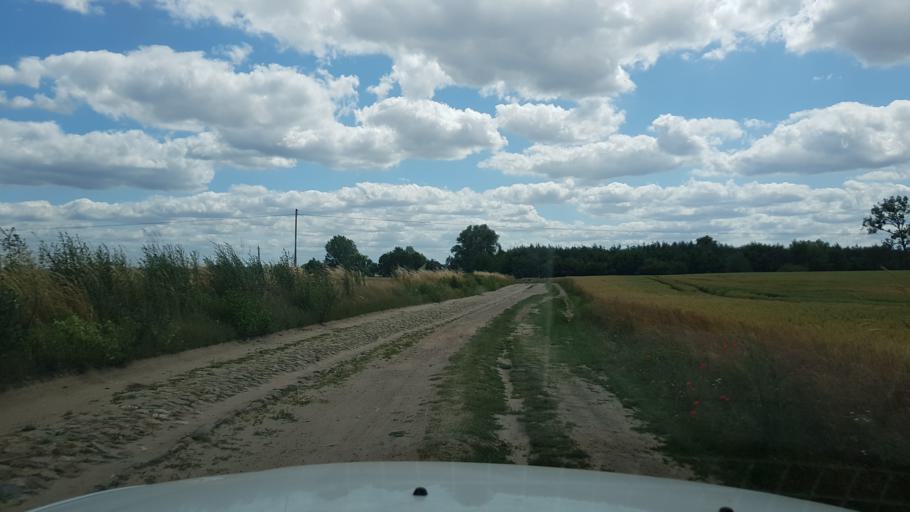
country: PL
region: West Pomeranian Voivodeship
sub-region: Powiat pyrzycki
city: Lipiany
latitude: 52.9668
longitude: 14.9910
